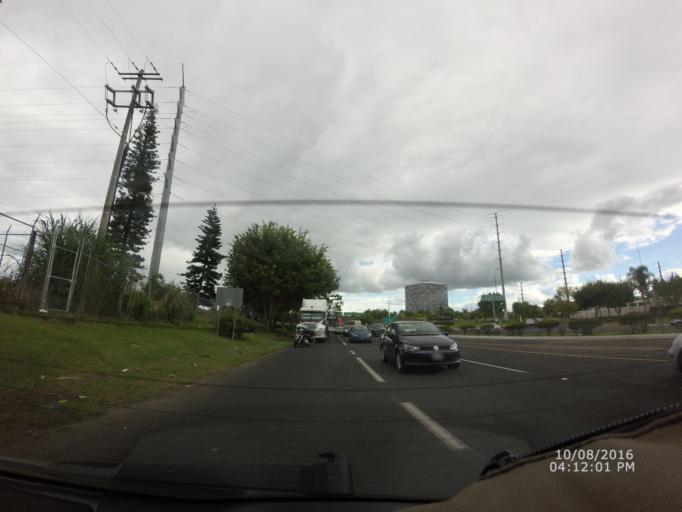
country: MX
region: Veracruz
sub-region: Xalapa
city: Colonia Santa Barbara
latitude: 19.5110
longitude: -96.8729
